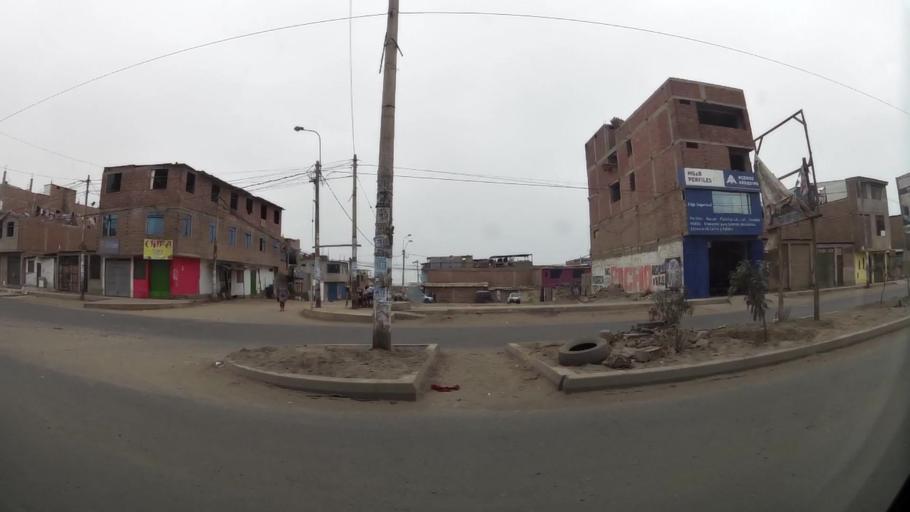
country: PE
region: Lima
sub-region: Lima
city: Punta Hermosa
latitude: -12.2415
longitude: -76.9155
